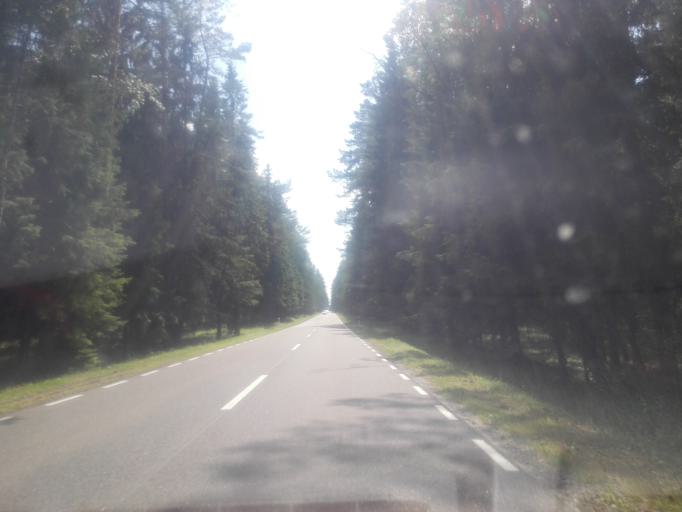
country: PL
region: Podlasie
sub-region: Powiat augustowski
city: Augustow
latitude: 53.9198
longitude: 23.1508
